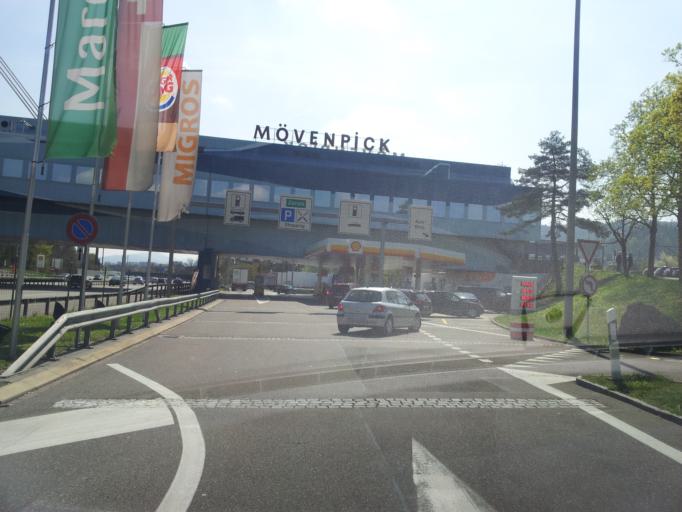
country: CH
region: Aargau
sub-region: Bezirk Baden
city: Killwangen
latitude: 47.4389
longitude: 8.3466
